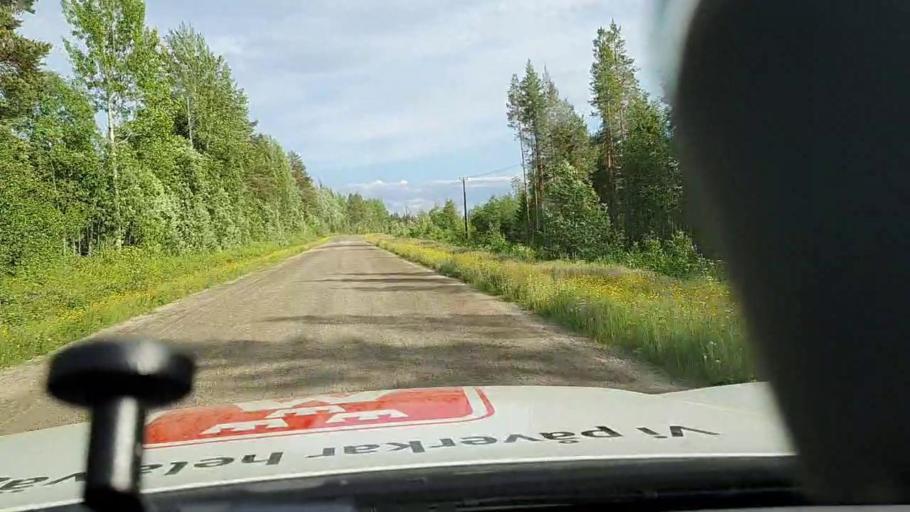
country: SE
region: Norrbotten
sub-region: Alvsbyns Kommun
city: AElvsbyn
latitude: 66.1780
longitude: 21.2354
